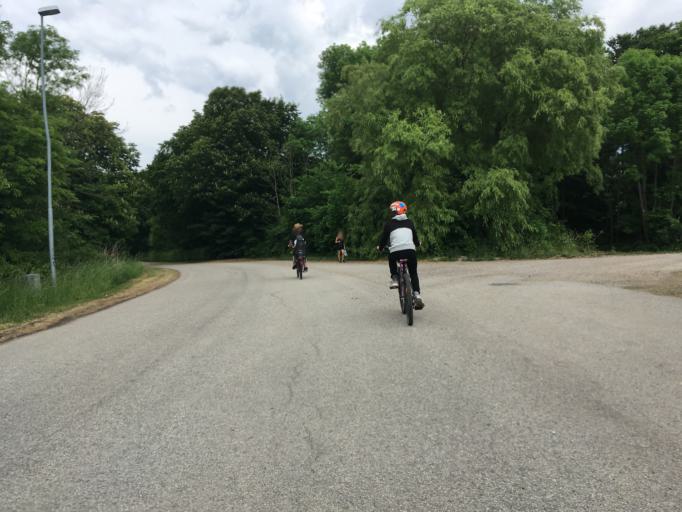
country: SE
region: Skane
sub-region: Staffanstorps Kommun
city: Hjaerup
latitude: 55.6992
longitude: 13.1415
